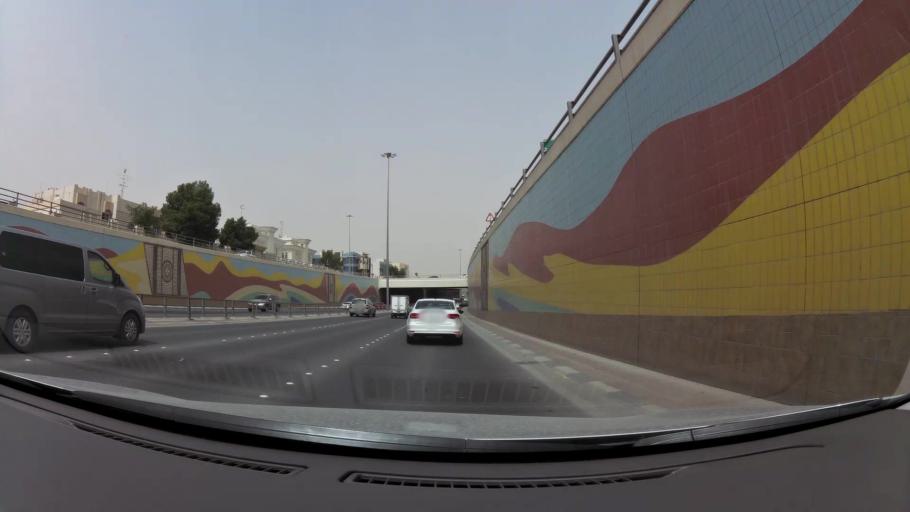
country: QA
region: Baladiyat ad Dawhah
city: Doha
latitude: 25.2586
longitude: 51.5012
